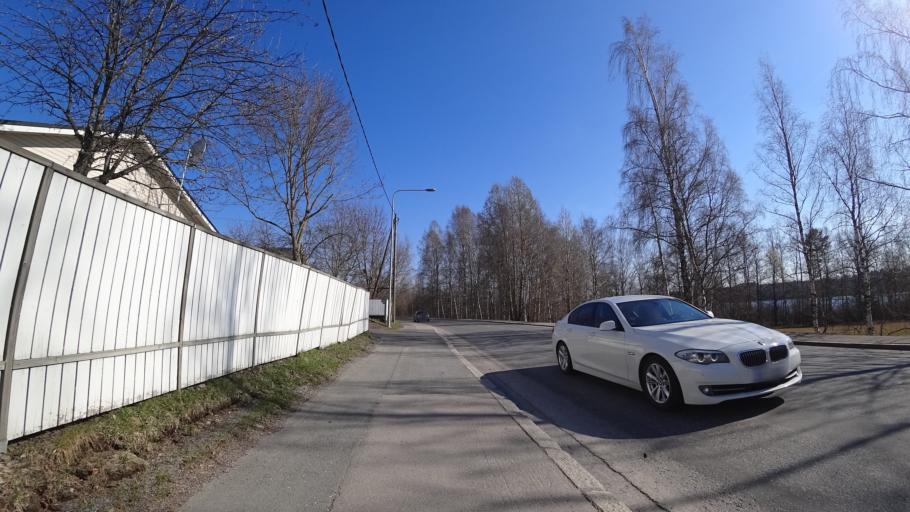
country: FI
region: Pirkanmaa
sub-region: Tampere
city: Pirkkala
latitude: 61.5138
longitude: 23.6540
